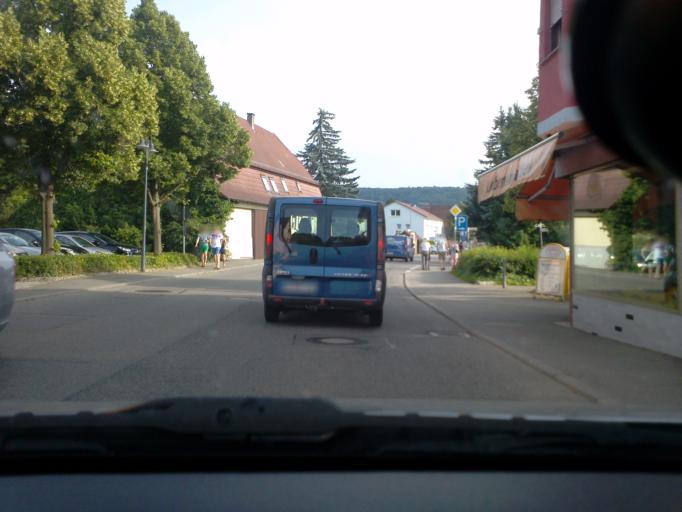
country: DE
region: Baden-Wuerttemberg
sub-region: Regierungsbezirk Stuttgart
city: Pfaffenhofen
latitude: 49.0633
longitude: 8.9751
